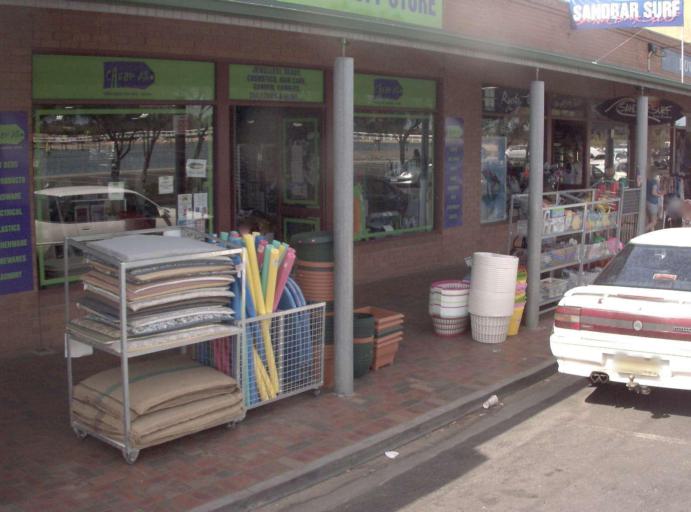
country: AU
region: Victoria
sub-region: East Gippsland
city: Lakes Entrance
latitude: -37.8796
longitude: 147.9915
